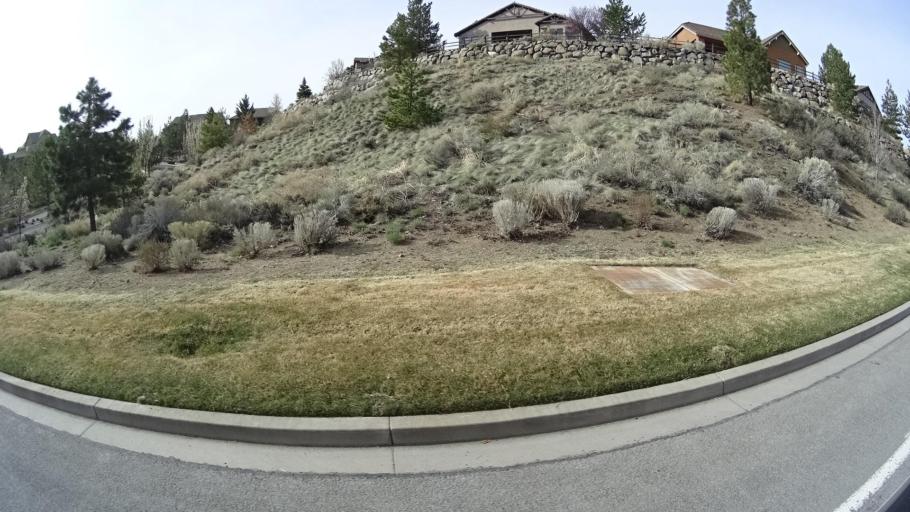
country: US
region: Nevada
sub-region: Washoe County
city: Mogul
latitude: 39.5370
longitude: -119.9320
